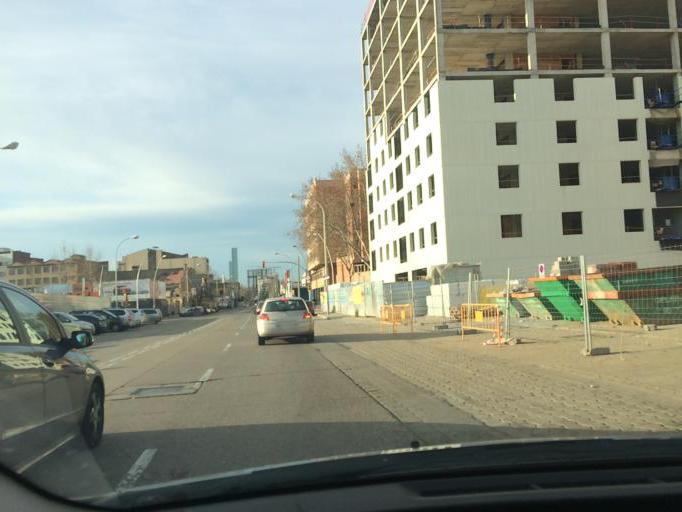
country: ES
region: Catalonia
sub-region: Provincia de Barcelona
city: Sant Marti
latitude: 41.4160
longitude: 2.2078
